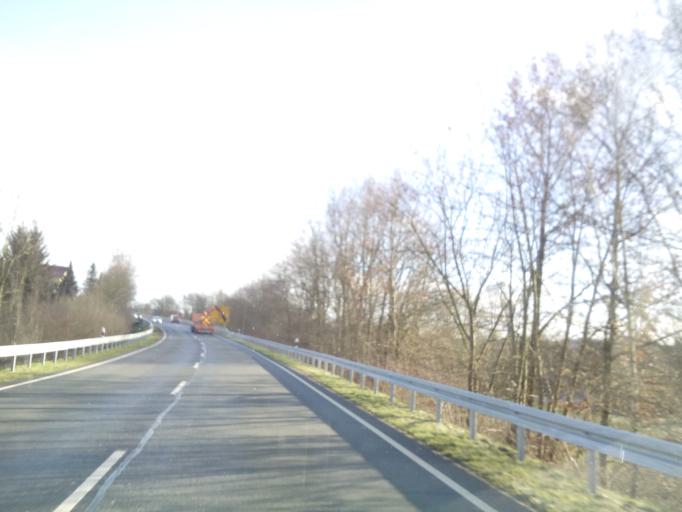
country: DE
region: Bavaria
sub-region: Upper Franconia
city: Mainleus
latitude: 50.1076
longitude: 11.3588
